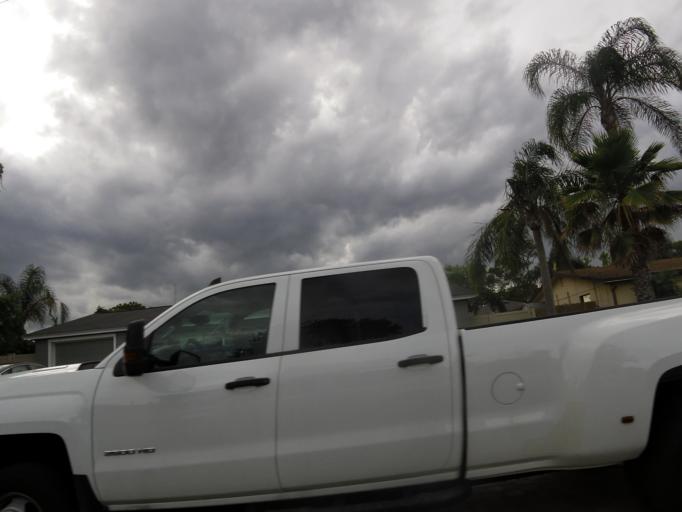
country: US
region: Florida
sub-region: Duval County
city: Jacksonville Beach
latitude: 30.2679
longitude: -81.3920
